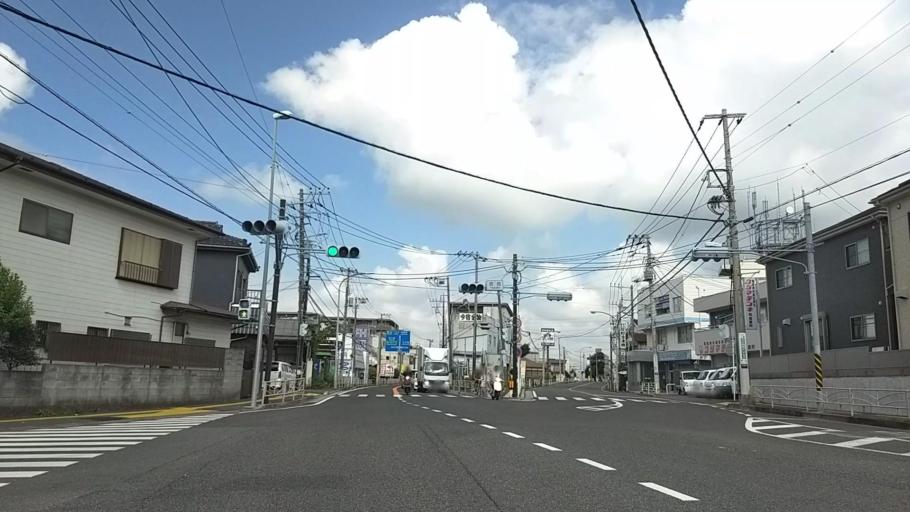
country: JP
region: Kanagawa
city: Minami-rinkan
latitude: 35.4839
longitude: 139.5256
